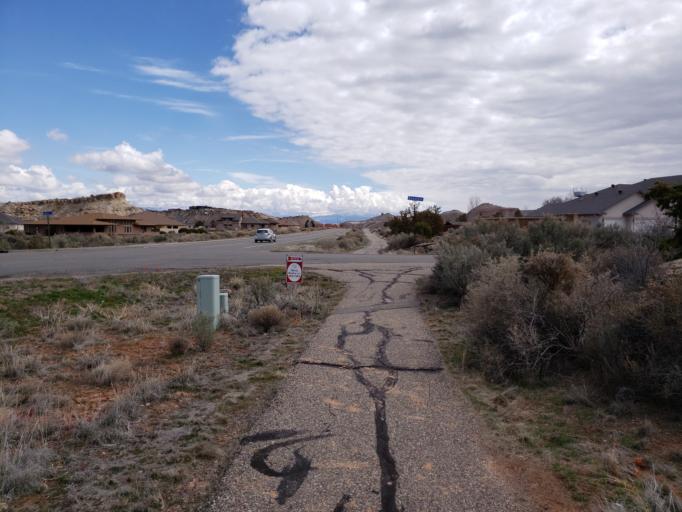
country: US
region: Colorado
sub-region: Mesa County
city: Redlands
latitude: 39.0533
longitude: -108.6416
